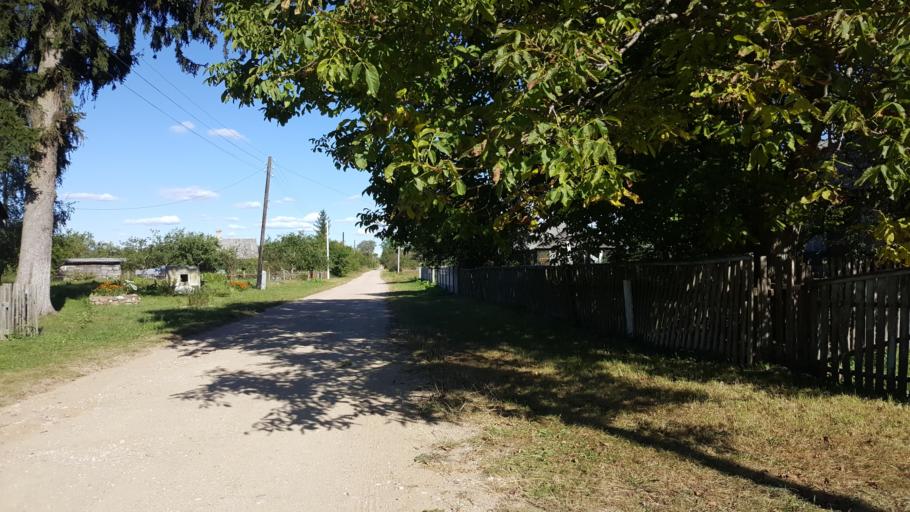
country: BY
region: Brest
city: Vysokaye
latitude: 52.3278
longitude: 23.5521
